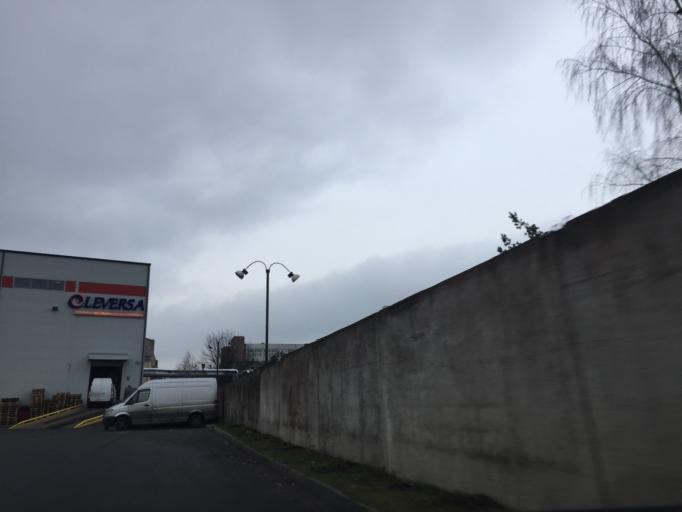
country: LV
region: Riga
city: Riga
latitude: 56.9922
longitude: 24.1156
